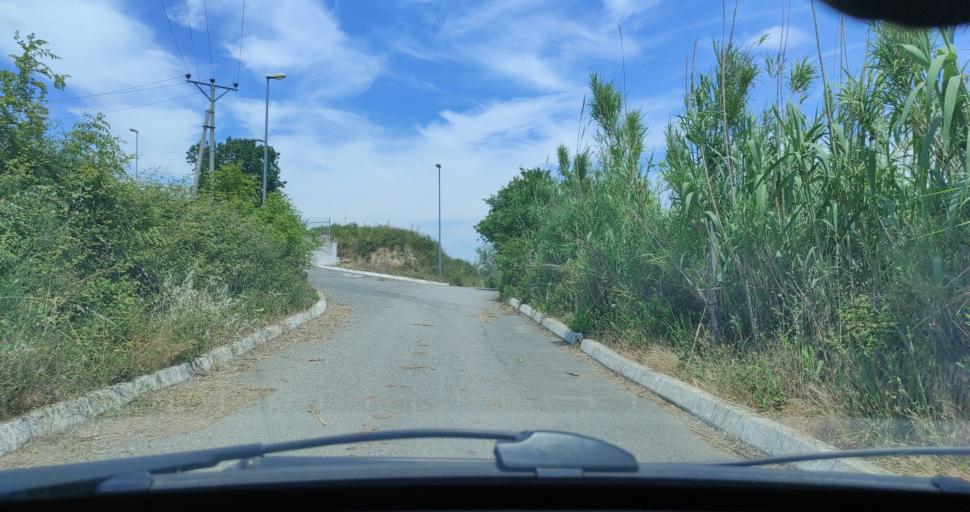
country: AL
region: Shkoder
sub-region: Rrethi i Shkodres
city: Velipoje
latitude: 41.8795
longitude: 19.3941
